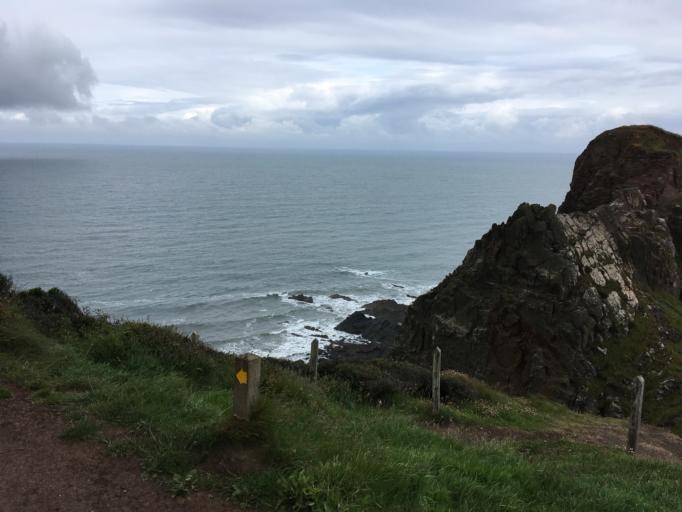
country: GB
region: England
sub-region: Cornwall
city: Flexbury
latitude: 51.0204
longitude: -4.5230
